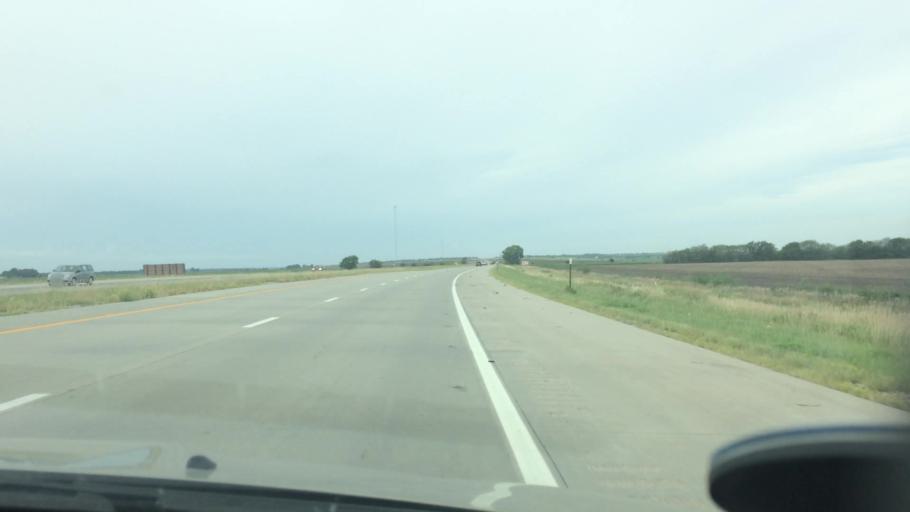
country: US
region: Kansas
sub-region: Dickinson County
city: Solomon
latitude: 38.9080
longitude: -97.4303
